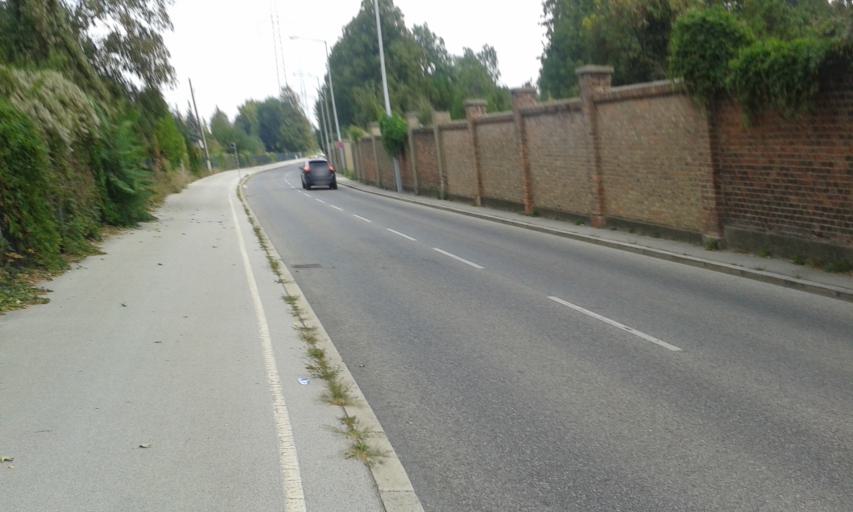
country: AT
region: Lower Austria
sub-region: Politischer Bezirk Wien-Umgebung
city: Schwechat
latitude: 48.1552
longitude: 16.4283
